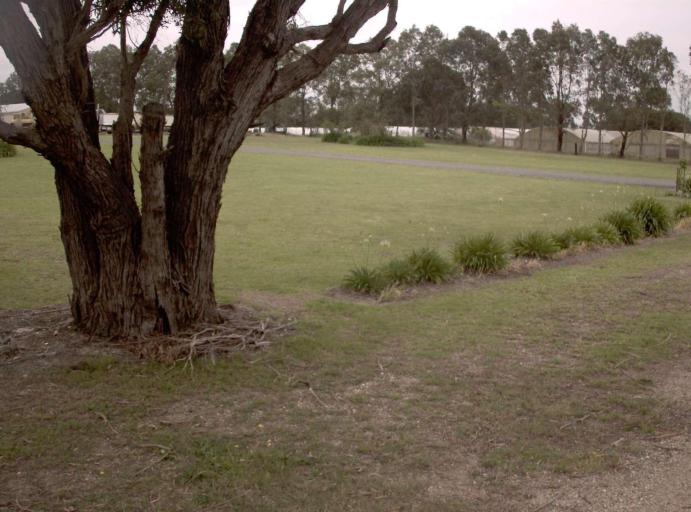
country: AU
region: Victoria
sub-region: East Gippsland
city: Bairnsdale
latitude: -37.8048
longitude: 147.4386
